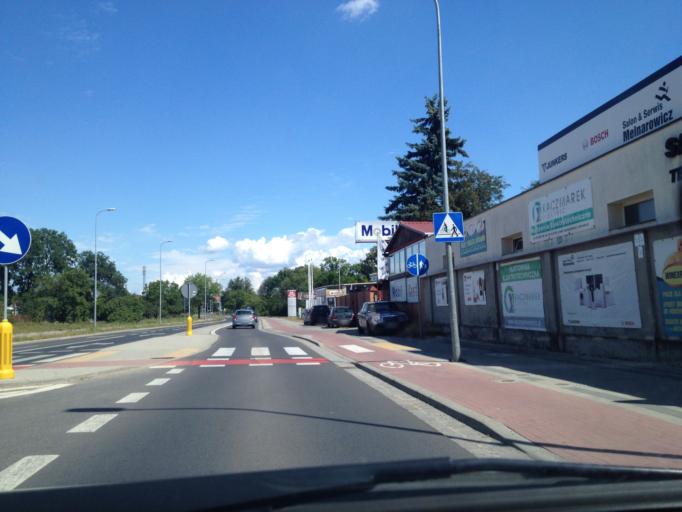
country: PL
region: Lower Silesian Voivodeship
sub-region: Legnica
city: Legnica
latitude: 51.1871
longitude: 16.1534
